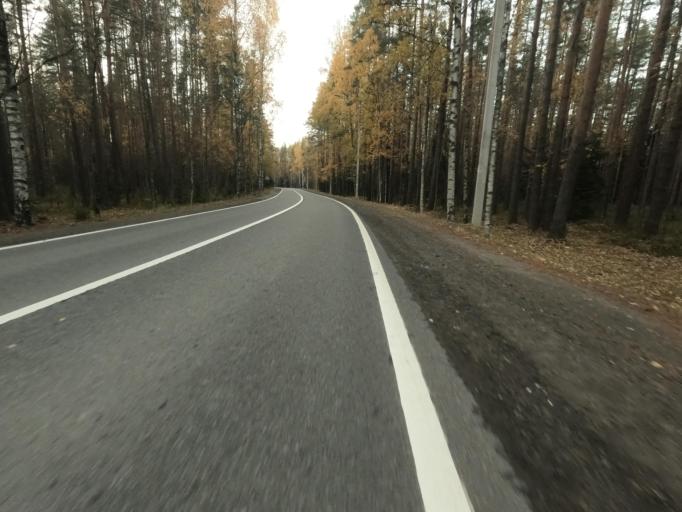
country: RU
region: St.-Petersburg
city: Repino
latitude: 60.1893
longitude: 29.8633
